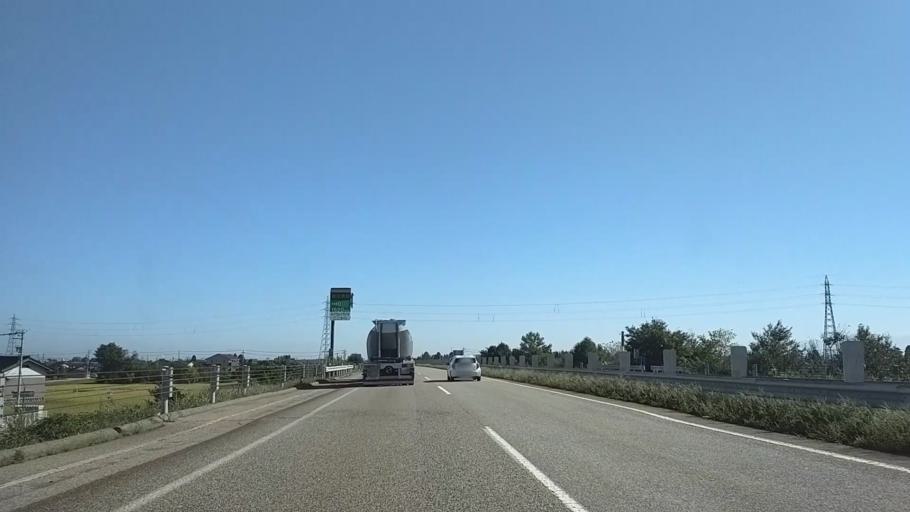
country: JP
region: Toyama
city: Nanto-shi
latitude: 36.6283
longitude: 136.9618
